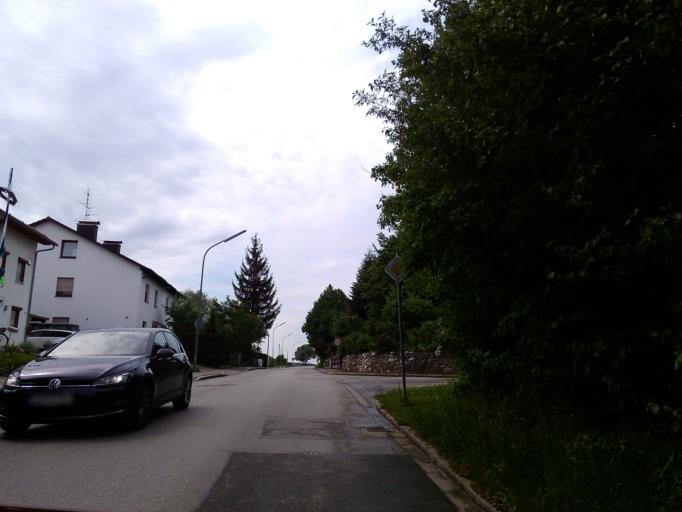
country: DE
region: Bavaria
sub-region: Upper Bavaria
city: Gauting
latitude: 48.0574
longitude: 11.4014
